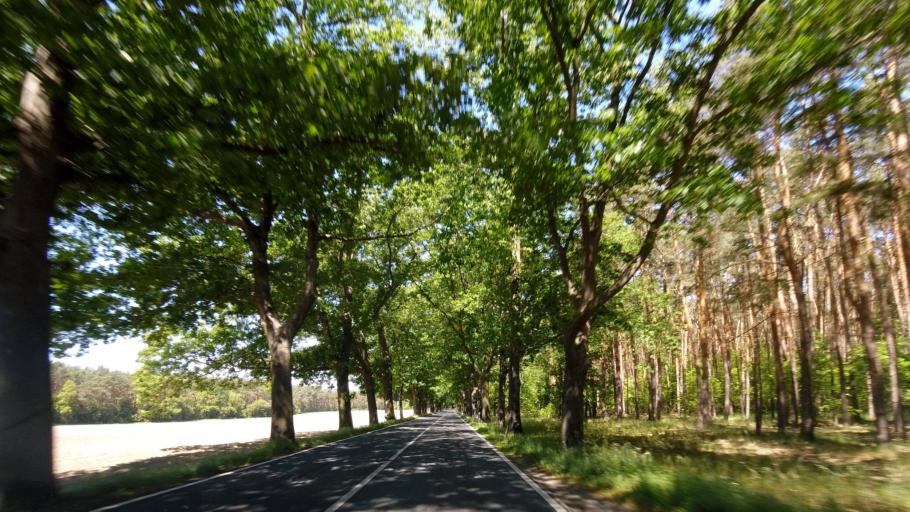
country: DE
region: Brandenburg
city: Trebbin
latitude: 52.2635
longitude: 13.2277
